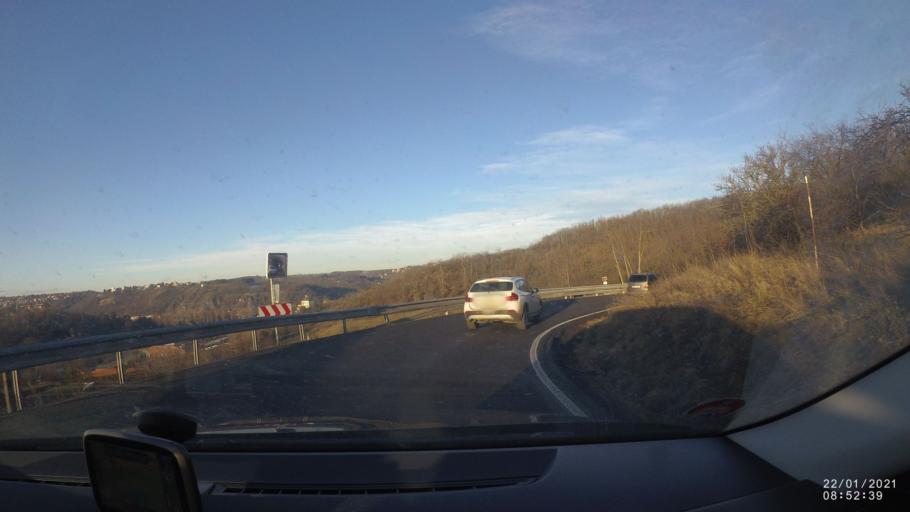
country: CZ
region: Praha
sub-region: Praha 1
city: Mala Strana
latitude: 50.1212
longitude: 14.4114
